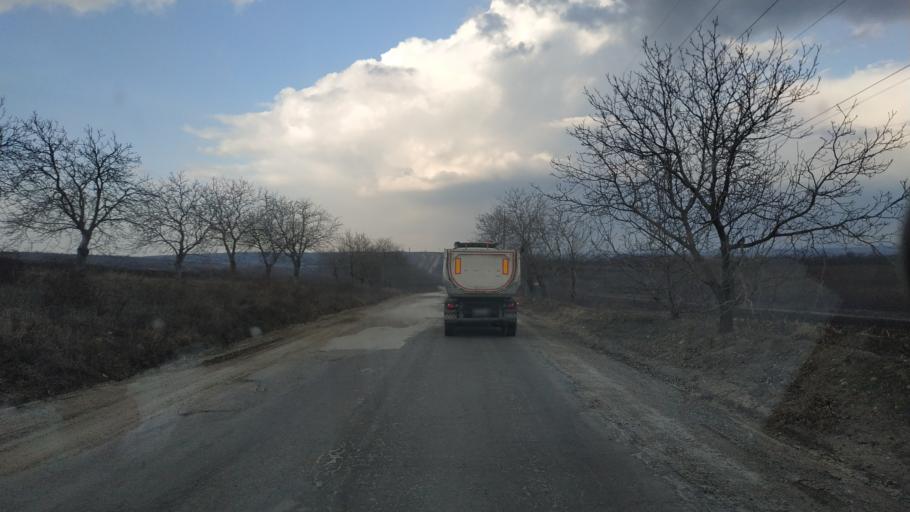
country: MD
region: Anenii Noi
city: Anenii Noi
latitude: 46.9707
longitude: 29.2852
